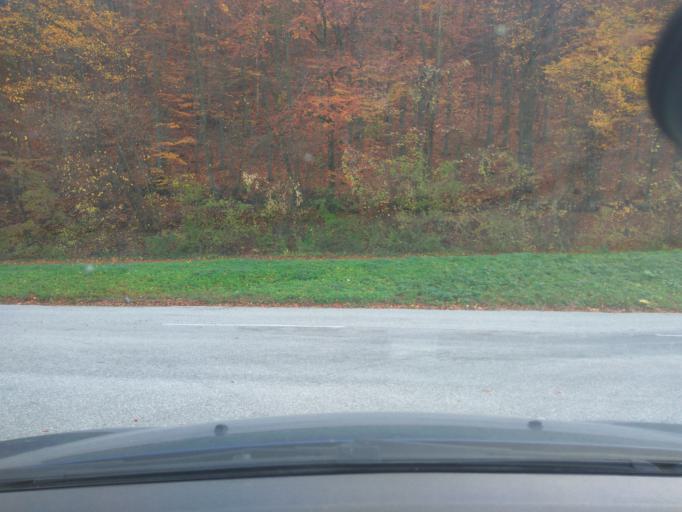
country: SK
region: Nitriansky
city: Brezova pod Bradlom
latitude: 48.6522
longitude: 17.5110
